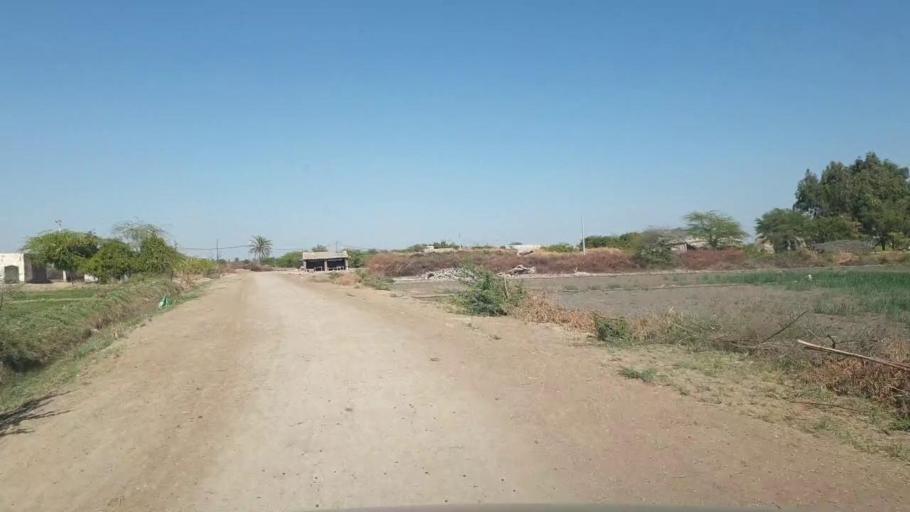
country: PK
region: Sindh
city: Dhoro Naro
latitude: 25.4330
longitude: 69.6134
